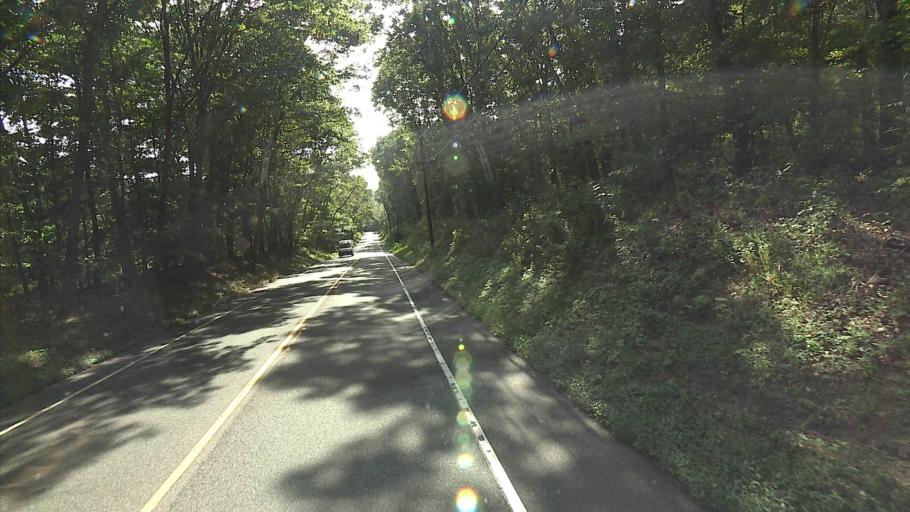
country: US
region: Connecticut
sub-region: New Haven County
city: Oxford
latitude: 41.3852
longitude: -73.1807
